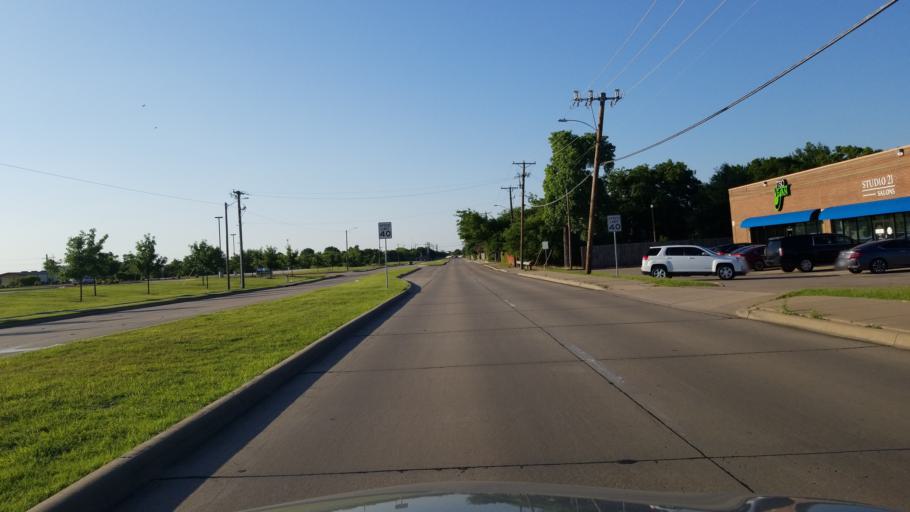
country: US
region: Texas
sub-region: Dallas County
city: Grand Prairie
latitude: 32.6921
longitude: -97.0183
